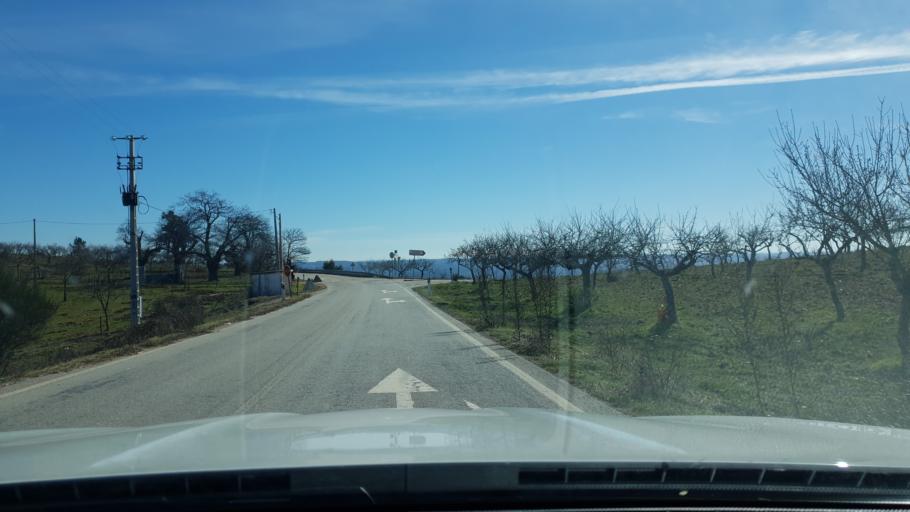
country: PT
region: Braganca
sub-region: Torre de Moncorvo
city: Torre de Moncorvo
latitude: 41.1801
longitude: -6.9363
